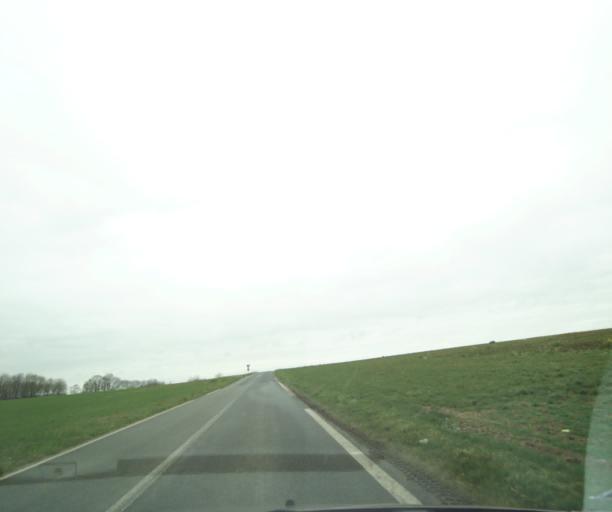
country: FR
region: Picardie
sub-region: Departement de l'Oise
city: Crisolles
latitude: 49.6018
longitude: 3.0111
